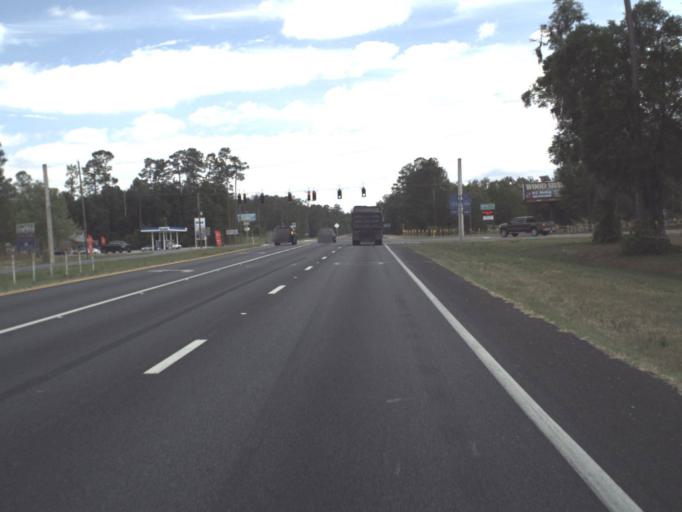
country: US
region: Florida
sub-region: Levy County
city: Williston
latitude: 29.2833
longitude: -82.3379
